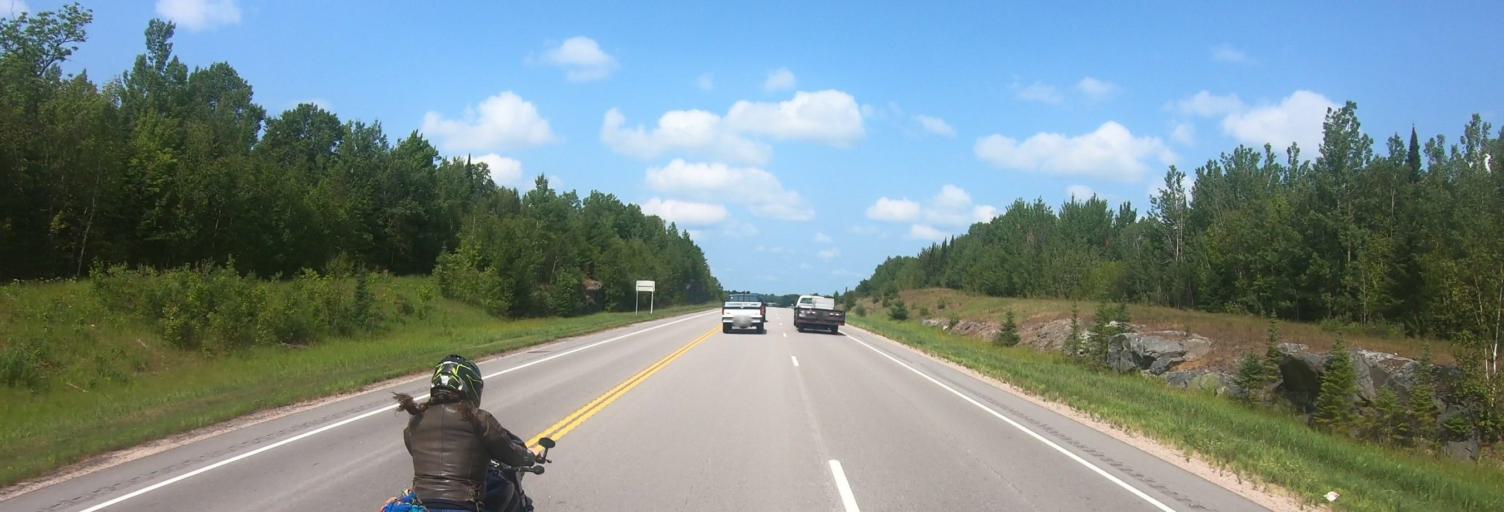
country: US
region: Minnesota
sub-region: Saint Louis County
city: Mountain Iron
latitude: 47.9136
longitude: -92.8069
